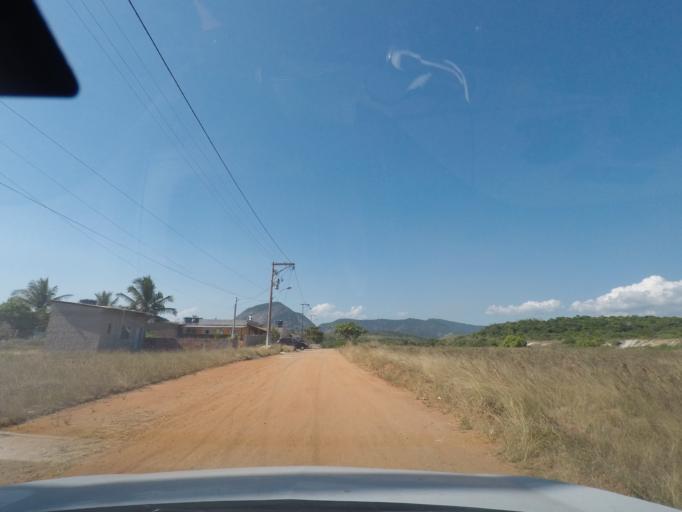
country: BR
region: Rio de Janeiro
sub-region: Marica
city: Marica
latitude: -22.9668
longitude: -42.9038
